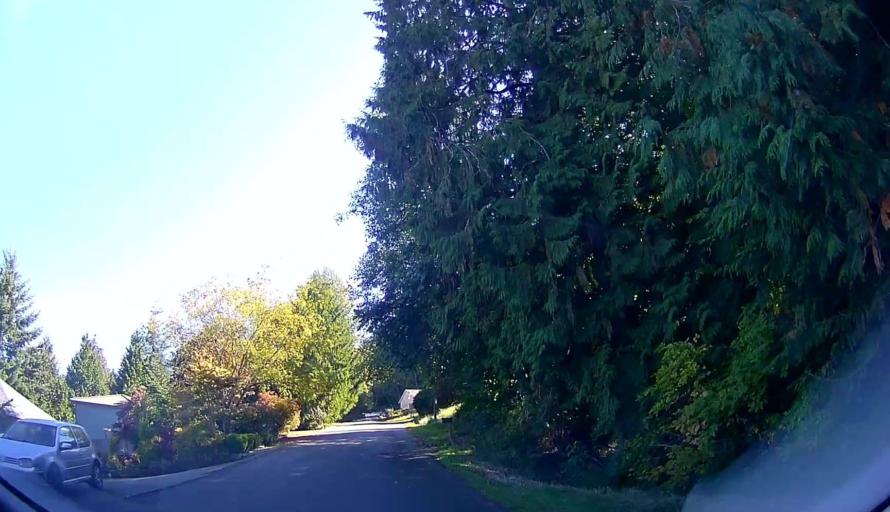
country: US
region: Washington
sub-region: Skagit County
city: Big Lake
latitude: 48.4326
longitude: -122.2782
